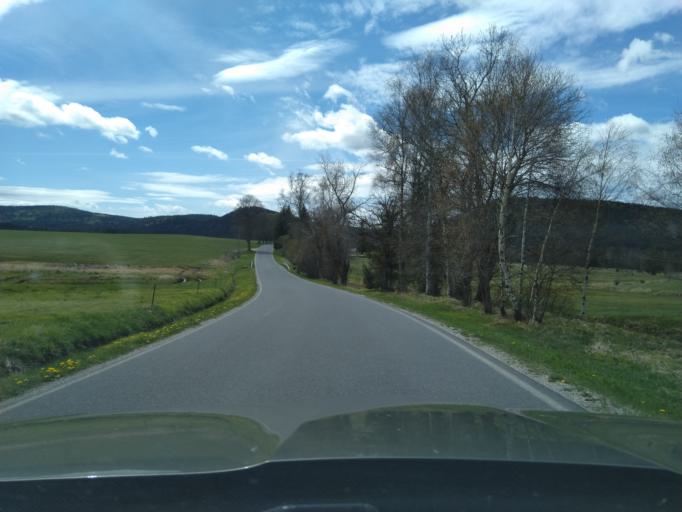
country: CZ
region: Jihocesky
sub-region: Okres Prachatice
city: Borova Lada
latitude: 48.9983
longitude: 13.6699
